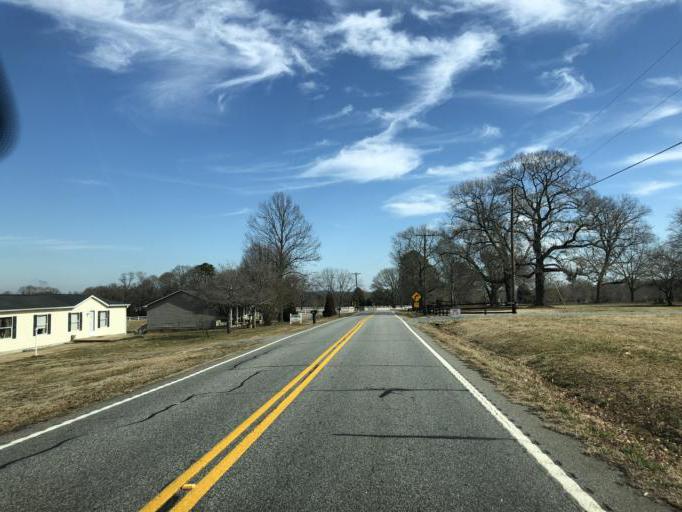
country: US
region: South Carolina
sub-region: Spartanburg County
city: Mayo
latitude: 35.0531
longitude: -81.9067
